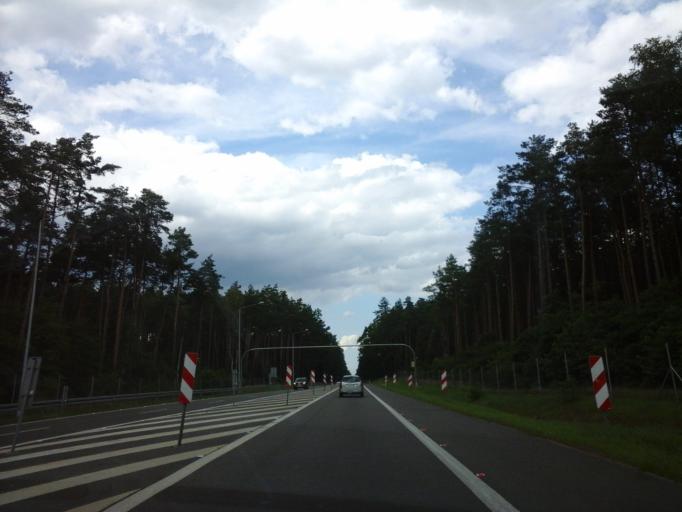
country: PL
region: West Pomeranian Voivodeship
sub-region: Powiat goleniowski
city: Goleniow
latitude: 53.6297
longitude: 14.8184
